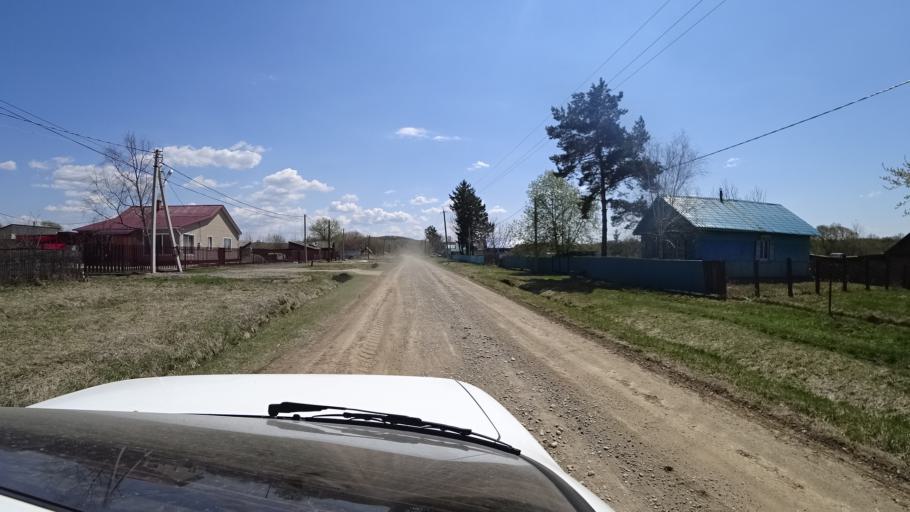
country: RU
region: Primorskiy
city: Lazo
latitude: 45.7928
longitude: 133.7639
